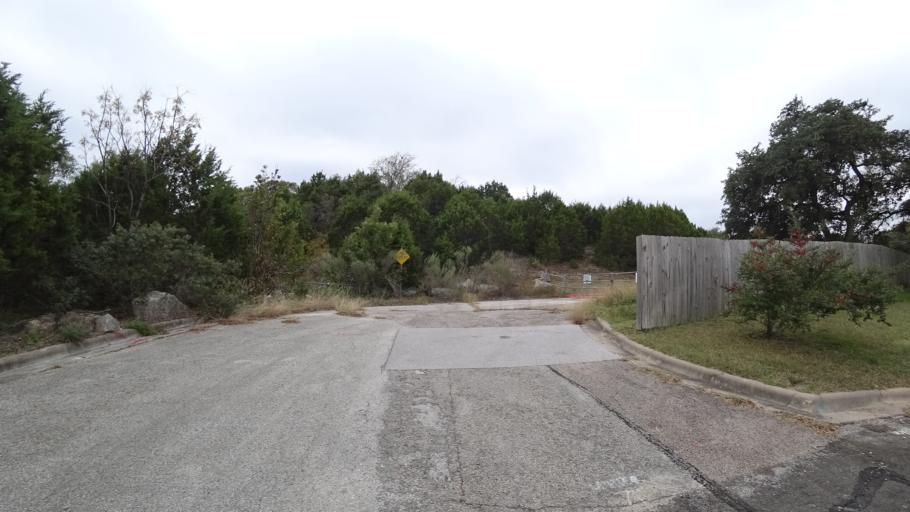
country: US
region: Texas
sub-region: Travis County
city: Barton Creek
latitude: 30.2336
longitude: -97.8820
